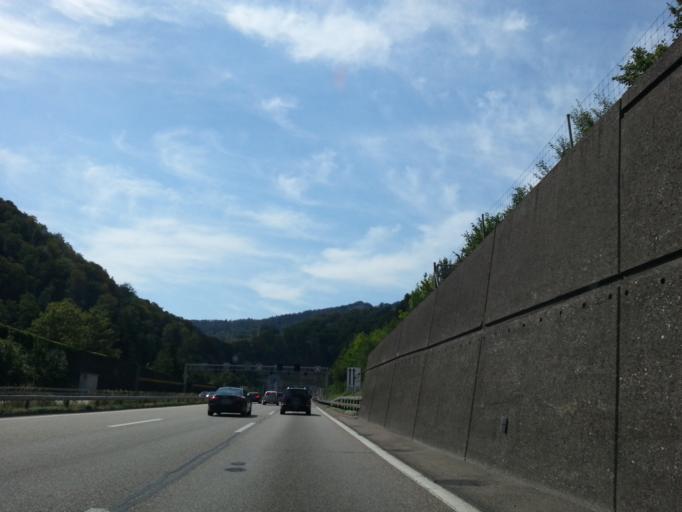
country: CH
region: Basel-Landschaft
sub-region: Bezirk Waldenburg
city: Diegten
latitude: 47.3851
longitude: 7.8170
